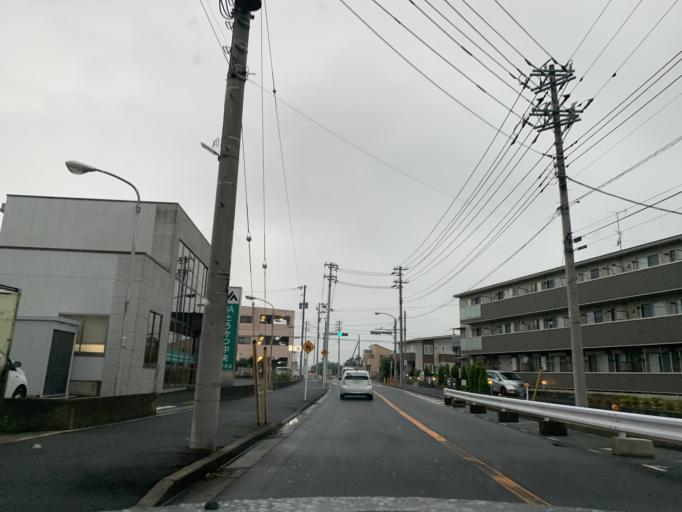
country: JP
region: Chiba
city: Nagareyama
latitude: 35.9104
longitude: 139.9036
